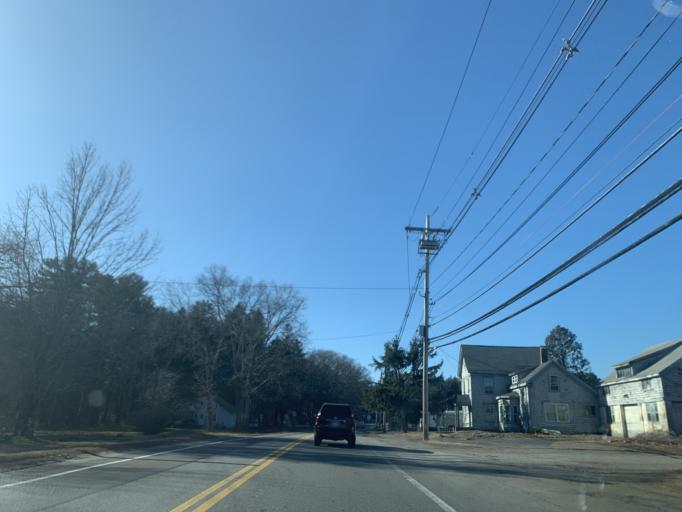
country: US
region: Massachusetts
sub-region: Middlesex County
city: Sudbury
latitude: 42.3603
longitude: -71.4335
